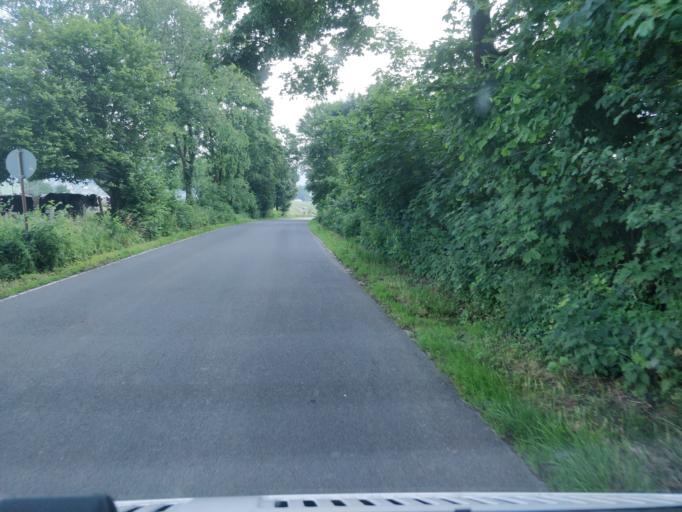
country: DE
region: North Rhine-Westphalia
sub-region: Regierungsbezirk Koln
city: Numbrecht
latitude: 50.9102
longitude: 7.5737
